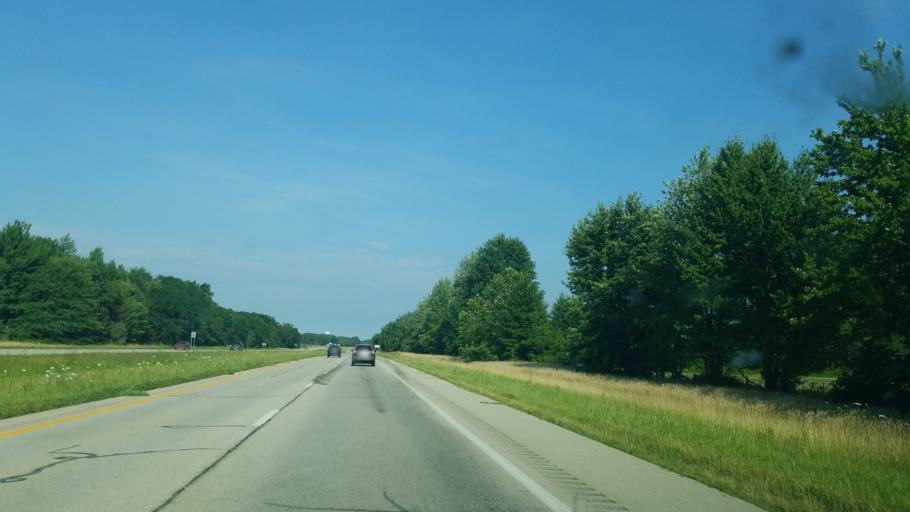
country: US
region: Ohio
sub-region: Clermont County
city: Williamsburg
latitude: 39.0617
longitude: -84.0198
